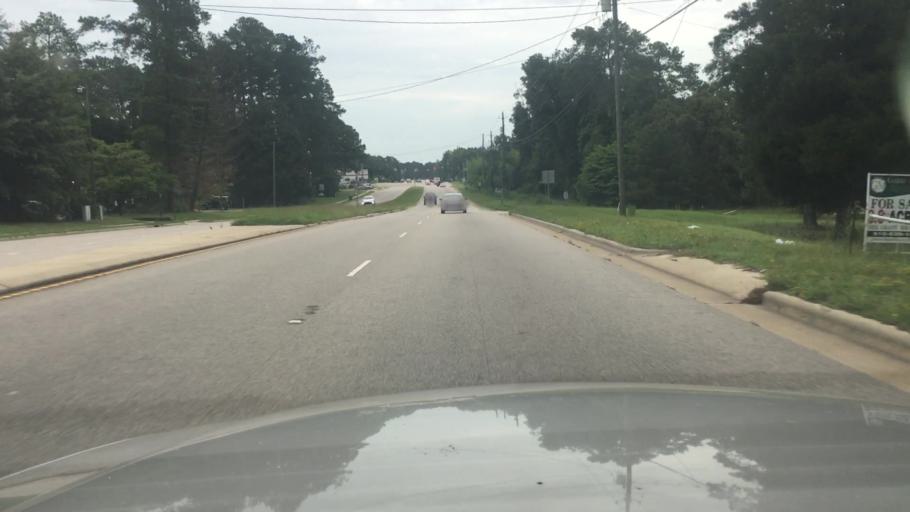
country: US
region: North Carolina
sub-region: Cumberland County
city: Hope Mills
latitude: 34.9980
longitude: -78.9716
